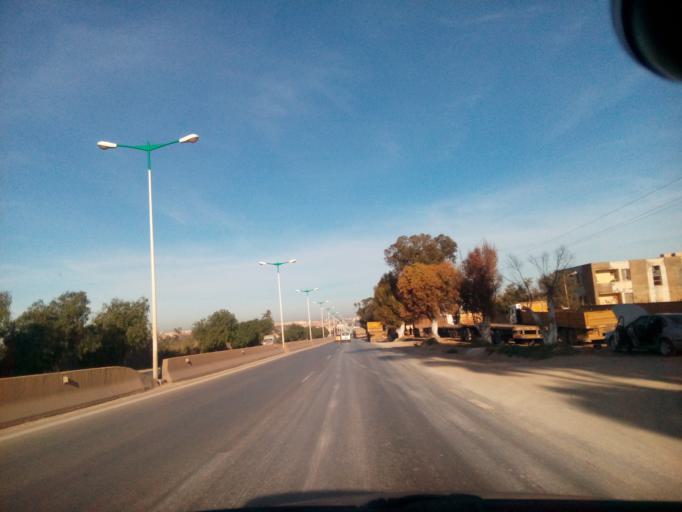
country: DZ
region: Mostaganem
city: Mostaganem
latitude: 35.8964
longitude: 0.1259
